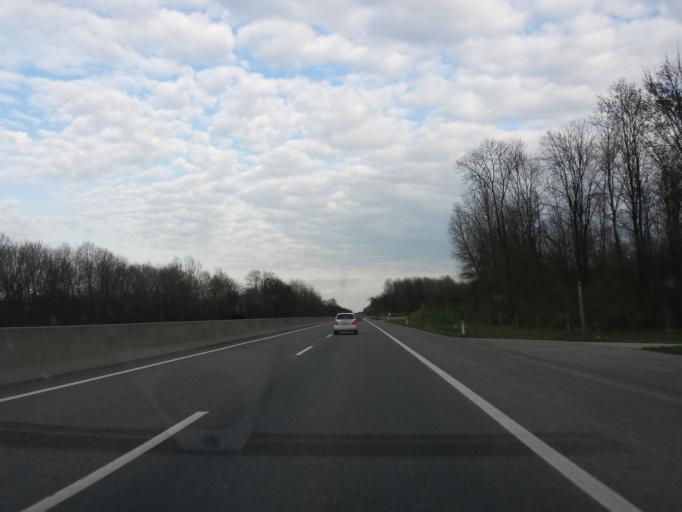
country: AT
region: Lower Austria
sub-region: Politischer Bezirk Korneuburg
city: Stetteldorf am Wagram
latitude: 48.3668
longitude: 15.9503
